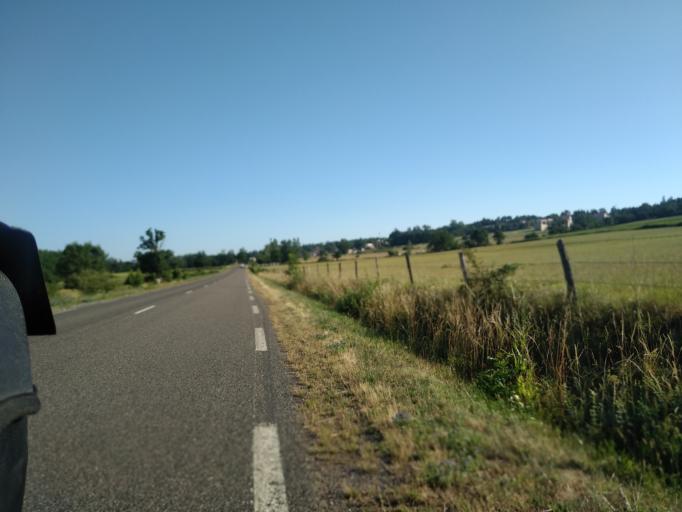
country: FR
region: Rhone-Alpes
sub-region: Departement de la Loire
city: Civens
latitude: 45.7525
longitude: 4.2707
